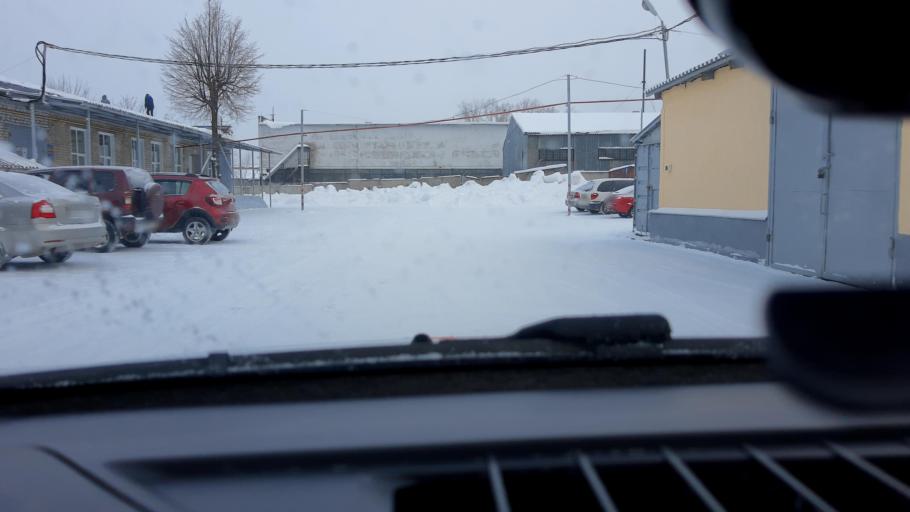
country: RU
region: Nizjnij Novgorod
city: Gorbatovka
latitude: 56.3375
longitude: 43.8121
